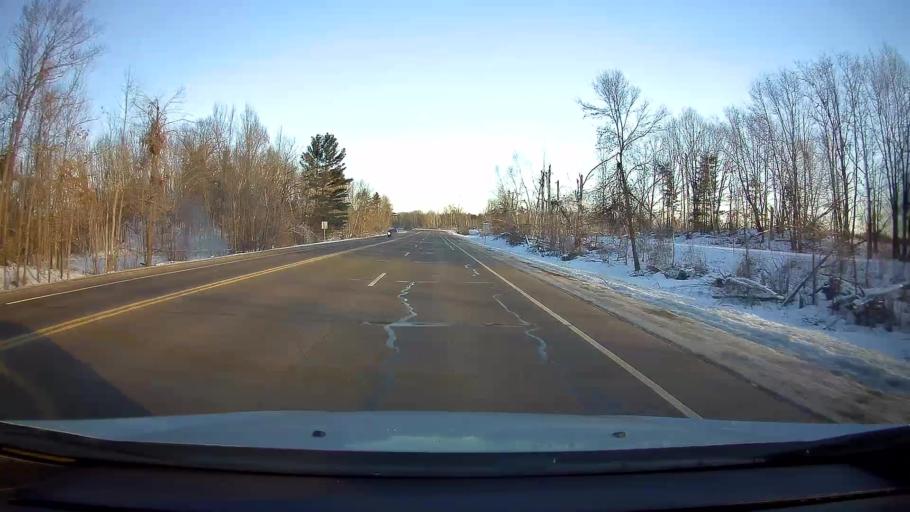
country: US
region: Wisconsin
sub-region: Barron County
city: Turtle Lake
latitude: 45.4272
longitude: -92.1295
